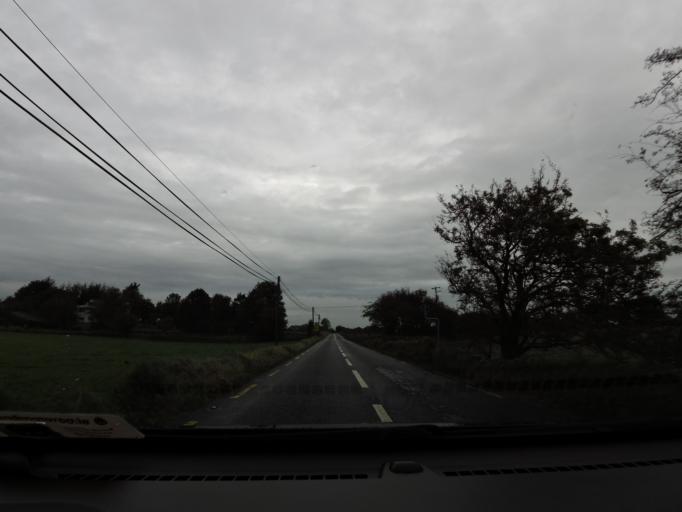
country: IE
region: Connaught
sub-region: County Galway
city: Tuam
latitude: 53.5391
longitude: -8.8170
